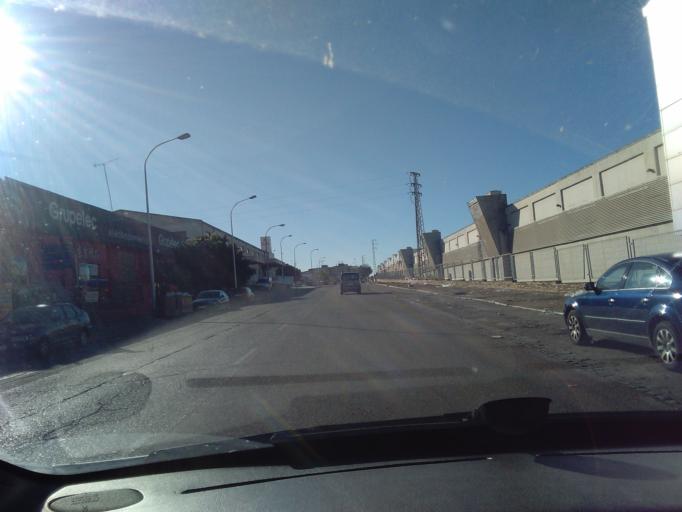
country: ES
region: Andalusia
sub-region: Provincia de Sevilla
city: Sevilla
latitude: 37.3923
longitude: -5.9496
